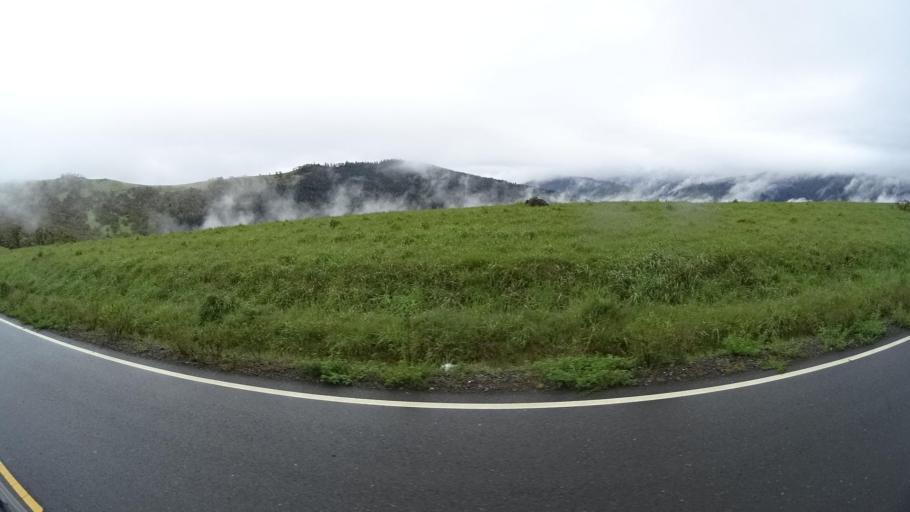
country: US
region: California
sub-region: Humboldt County
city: Westhaven-Moonstone
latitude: 41.1633
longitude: -123.9030
